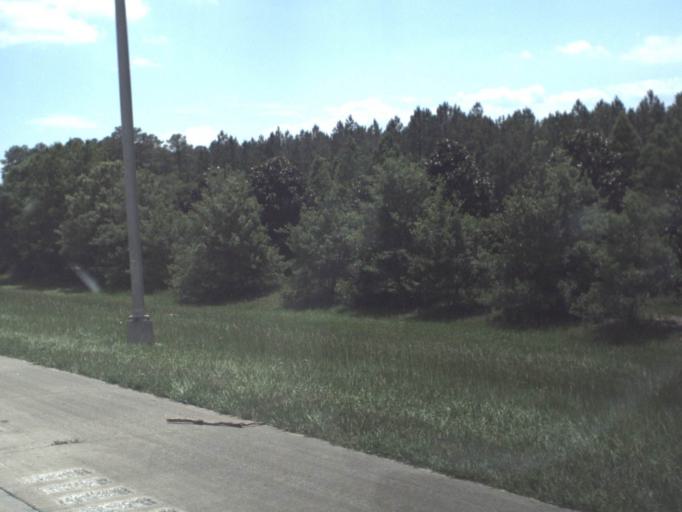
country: US
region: Florida
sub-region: Saint Johns County
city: Palm Valley
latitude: 30.1805
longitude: -81.5144
